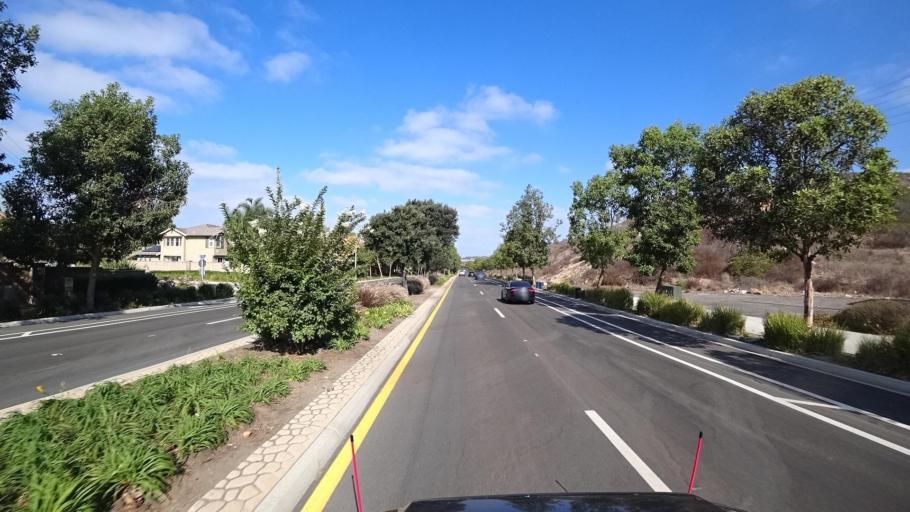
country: US
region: California
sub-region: San Diego County
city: Lake San Marcos
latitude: 33.0954
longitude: -117.2088
